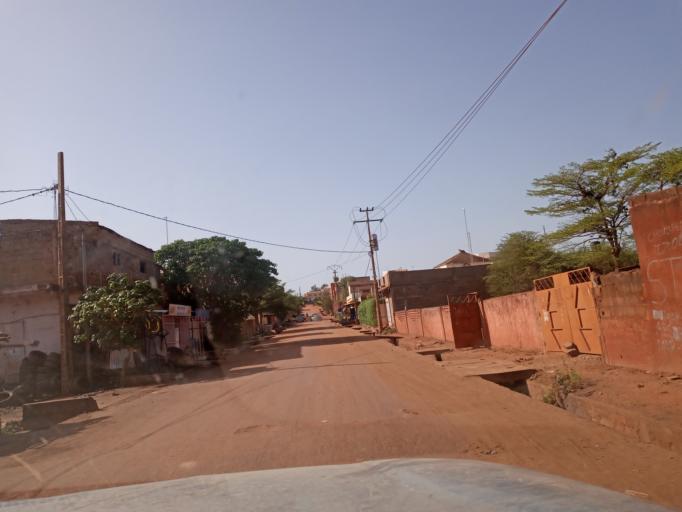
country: ML
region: Bamako
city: Bamako
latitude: 12.6709
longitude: -7.9178
